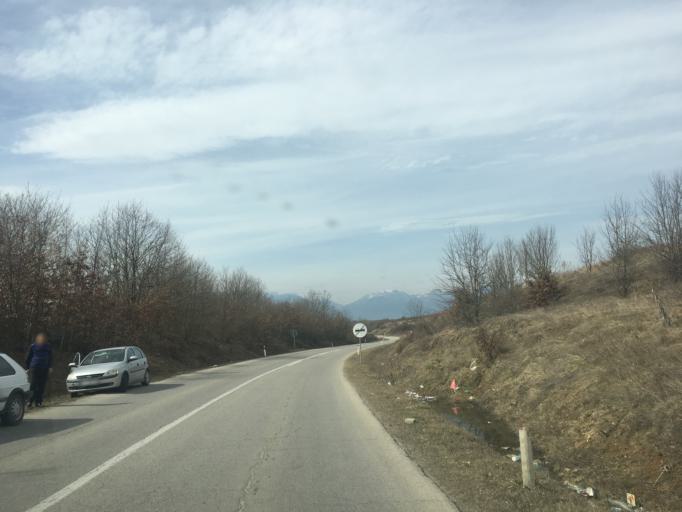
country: XK
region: Pec
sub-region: Komuna e Klines
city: Klina
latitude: 42.5923
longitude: 20.5494
